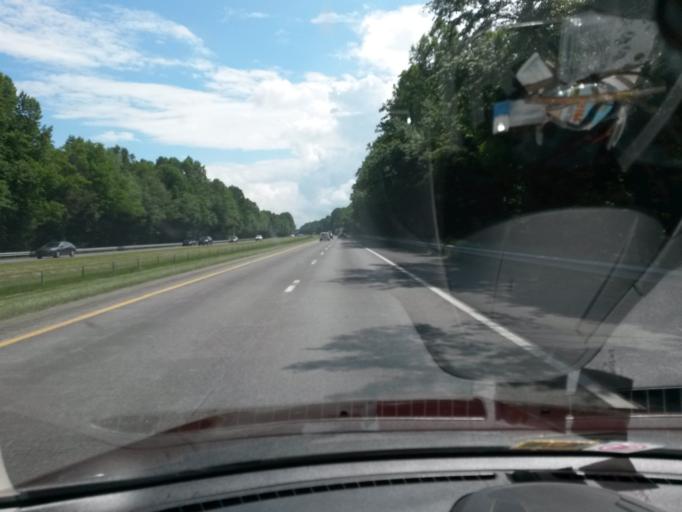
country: US
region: North Carolina
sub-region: Surry County
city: Dobson
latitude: 36.4068
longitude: -80.7831
